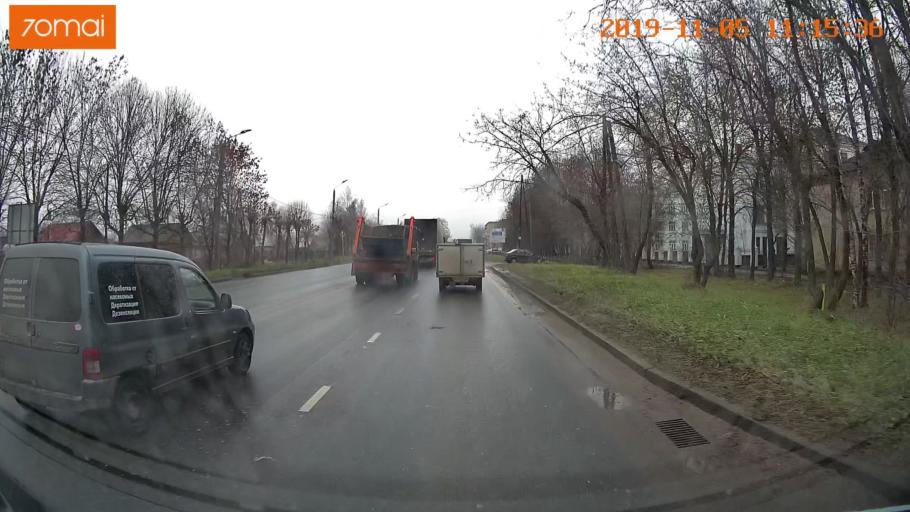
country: RU
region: Ivanovo
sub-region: Gorod Ivanovo
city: Ivanovo
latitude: 56.9784
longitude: 40.9541
